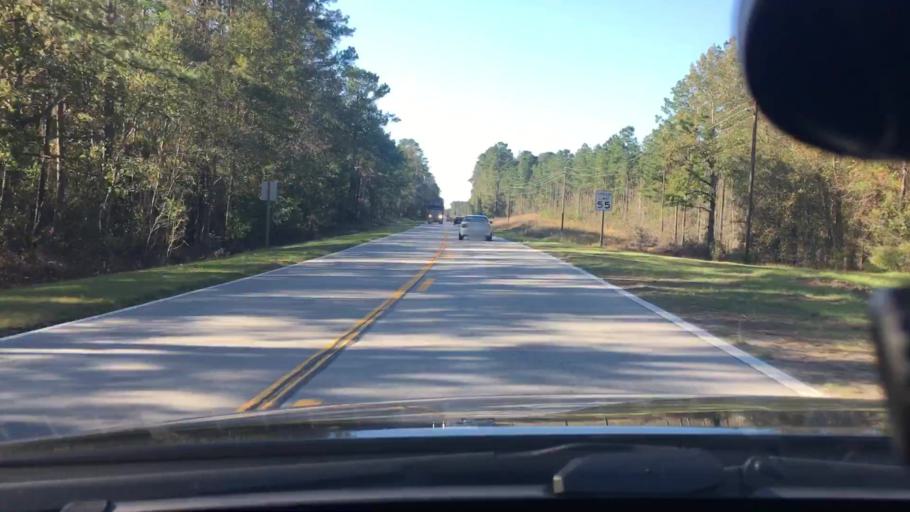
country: US
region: North Carolina
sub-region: Craven County
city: Vanceboro
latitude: 35.2188
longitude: -77.1225
